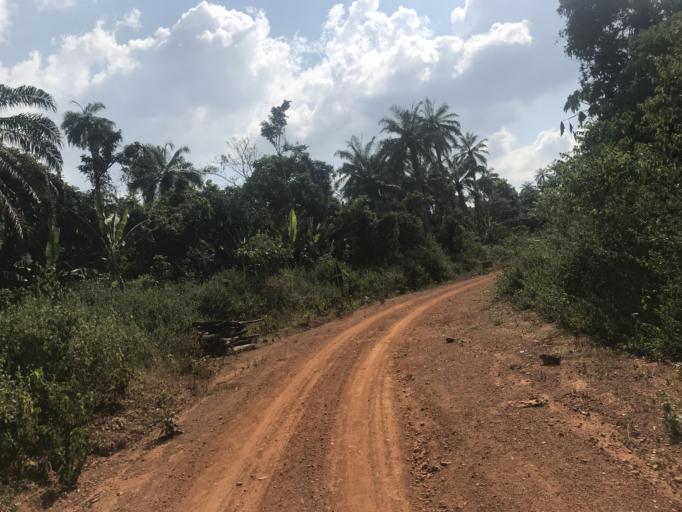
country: NG
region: Osun
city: Ibokun
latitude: 7.8166
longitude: 4.6975
